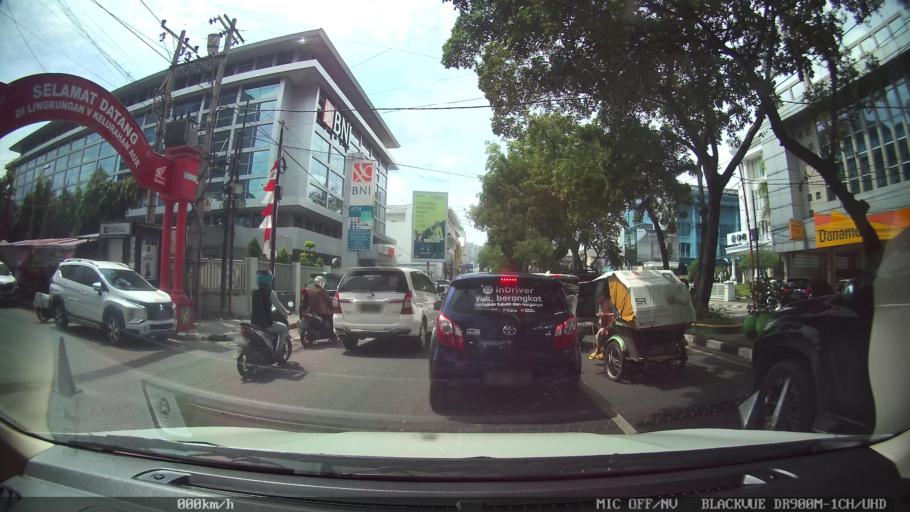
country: ID
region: North Sumatra
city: Medan
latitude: 3.5831
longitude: 98.6815
